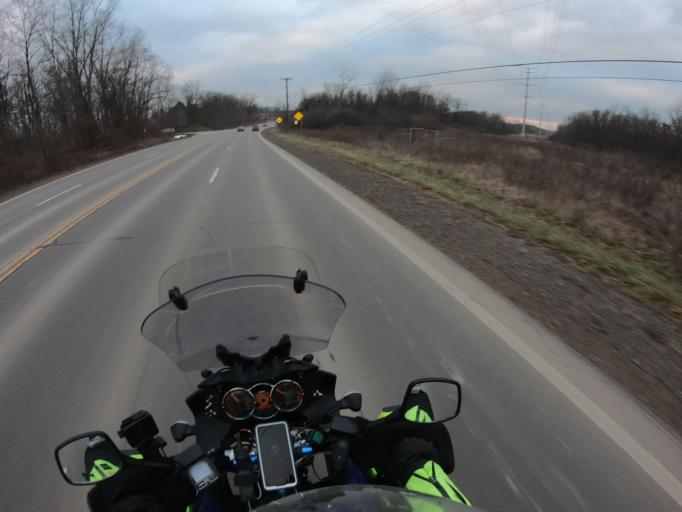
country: US
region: Michigan
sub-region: Oakland County
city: Holly
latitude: 42.8213
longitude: -83.5554
